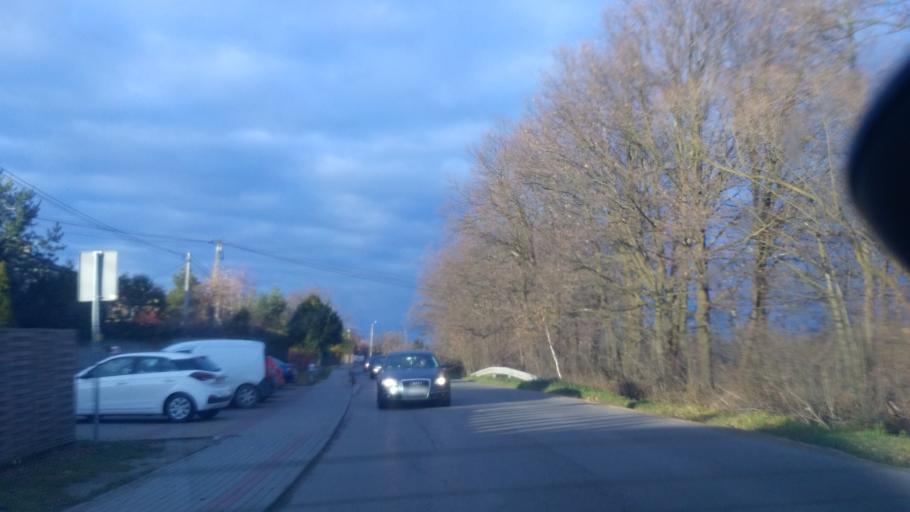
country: PL
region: Subcarpathian Voivodeship
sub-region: Powiat rzeszowski
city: Krasne
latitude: 50.0477
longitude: 22.1230
